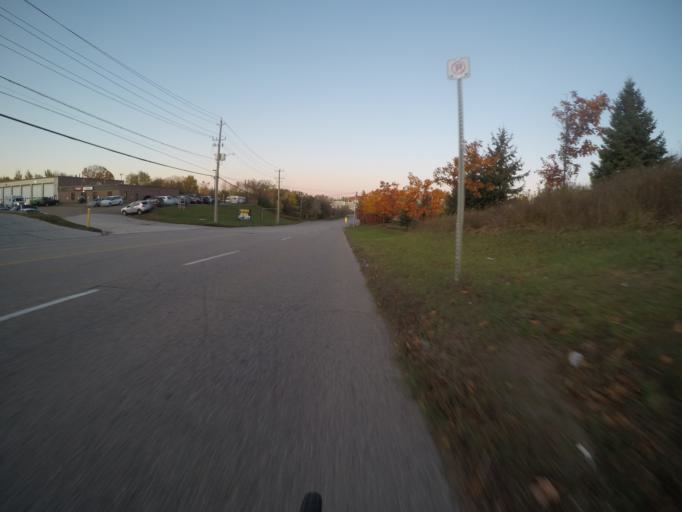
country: CA
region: Ontario
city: Kitchener
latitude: 43.4087
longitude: -80.4443
